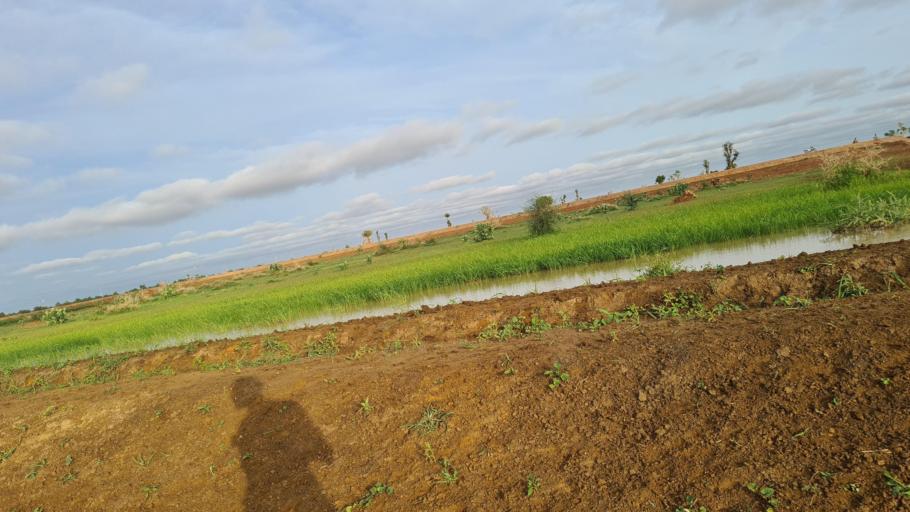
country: NE
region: Tahoua
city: Birni N Konni
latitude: 13.7869
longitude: 5.2316
